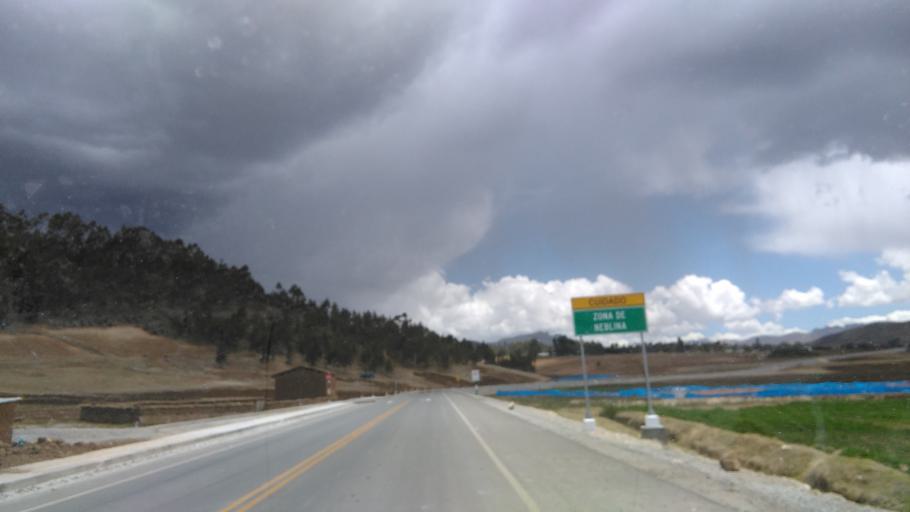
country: PE
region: Apurimac
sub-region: Provincia de Andahuaylas
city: San Jeronimo
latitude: -13.7160
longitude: -73.3497
